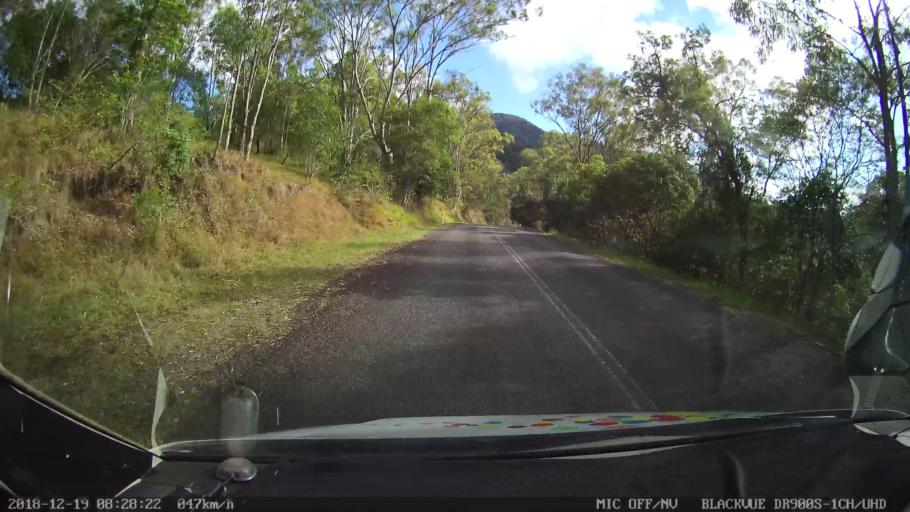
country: AU
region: New South Wales
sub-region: Kyogle
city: Kyogle
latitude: -28.3213
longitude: 152.9312
